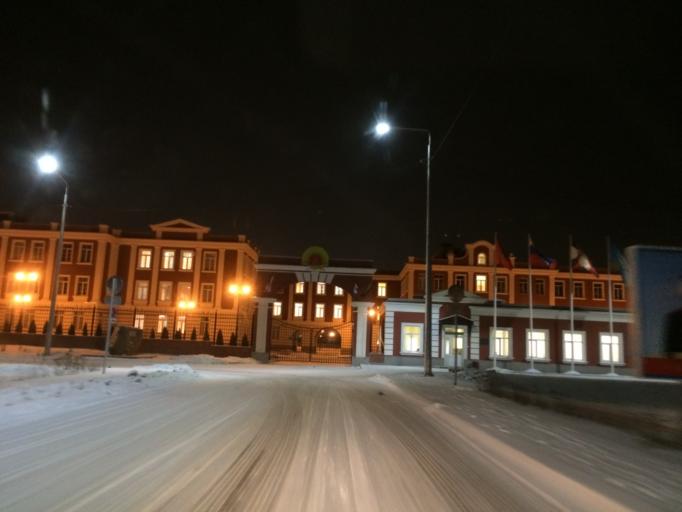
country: RU
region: Tula
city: Tula
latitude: 54.1886
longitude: 37.6530
